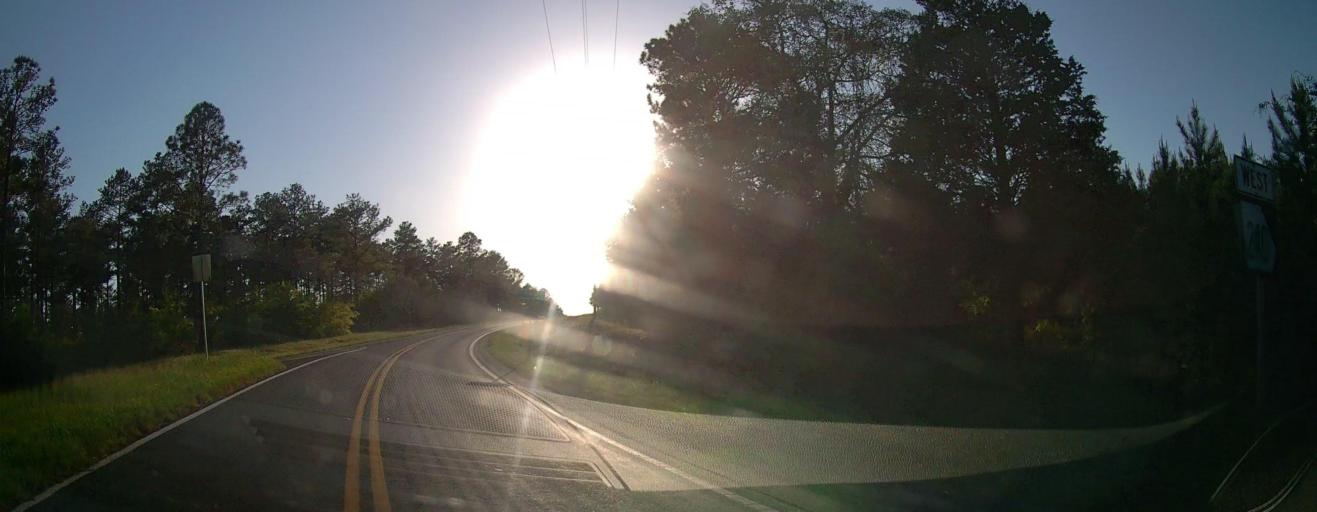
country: US
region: Georgia
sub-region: Schley County
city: Ellaville
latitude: 32.3218
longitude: -84.2217
